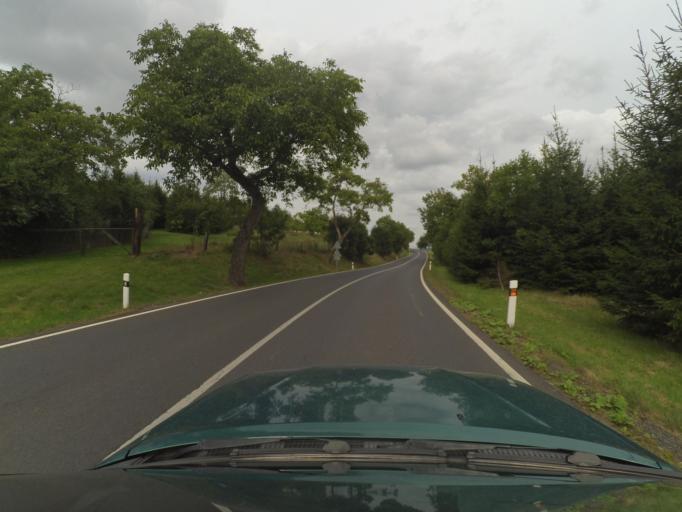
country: CZ
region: Ustecky
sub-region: Okres Louny
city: Louny
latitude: 50.2863
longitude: 13.7784
